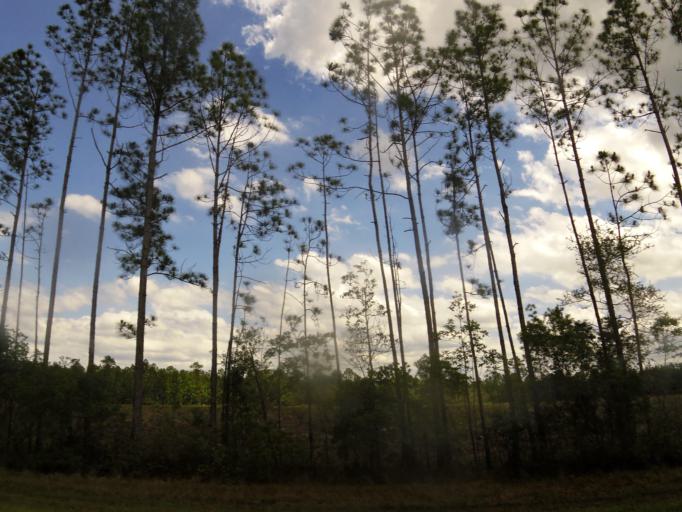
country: US
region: Florida
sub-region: Clay County
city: Green Cove Springs
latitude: 29.9198
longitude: -81.7620
